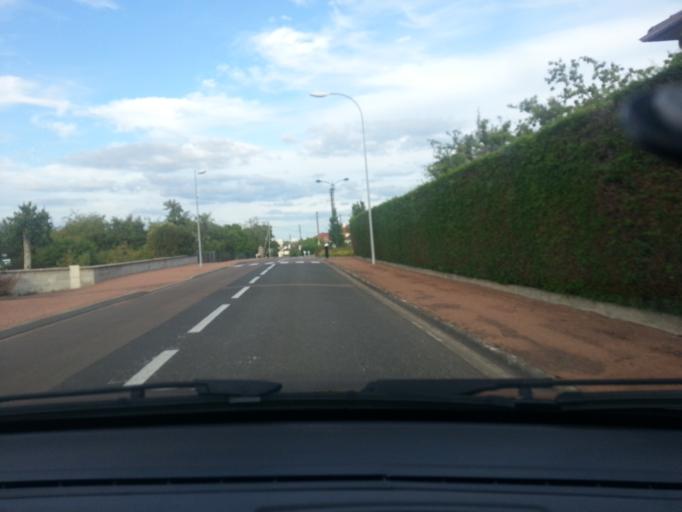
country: FR
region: Bourgogne
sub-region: Departement de Saone-et-Loire
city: Chatenoy-le-Royal
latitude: 46.8021
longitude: 4.8068
